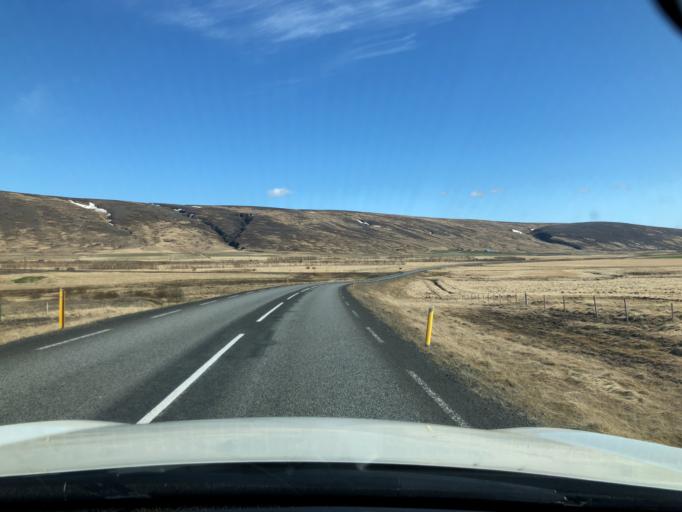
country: IS
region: South
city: Hveragerdi
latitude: 64.6948
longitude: -21.2392
